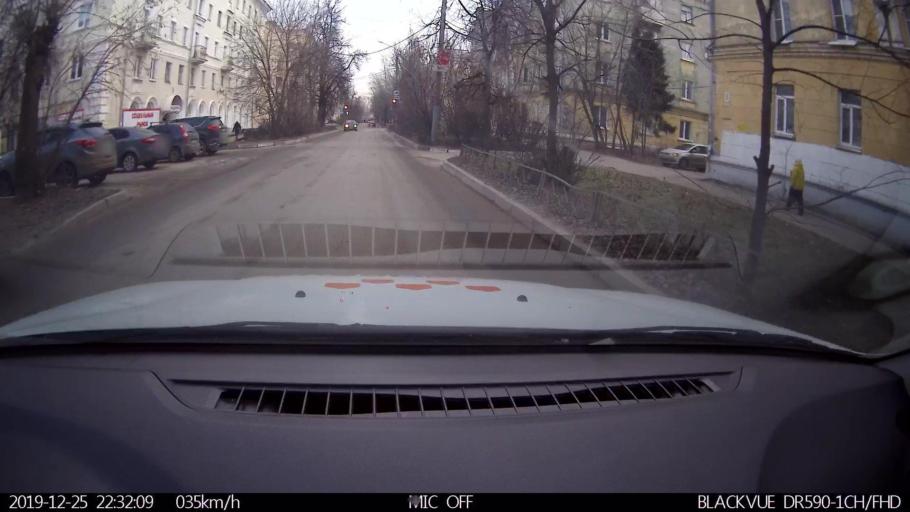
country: RU
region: Nizjnij Novgorod
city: Nizhniy Novgorod
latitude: 56.3355
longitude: 43.8801
